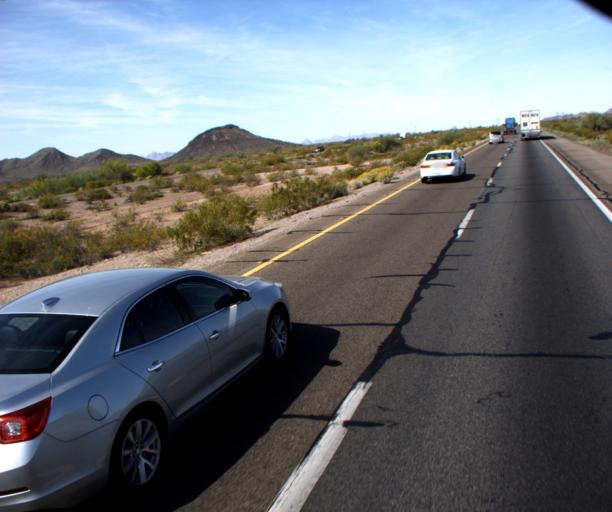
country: US
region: Arizona
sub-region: Maricopa County
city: Buckeye
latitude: 33.5087
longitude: -112.9980
